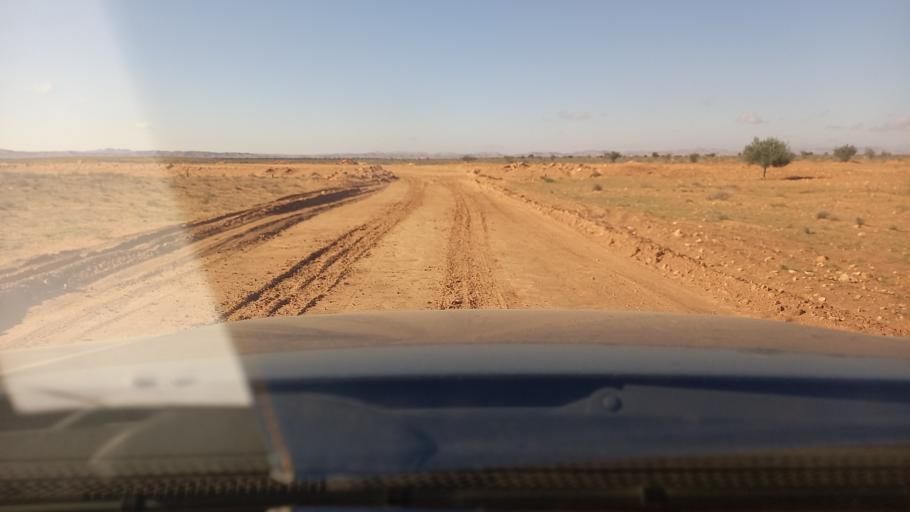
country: TN
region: Madanin
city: Medenine
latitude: 33.1726
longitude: 10.5276
